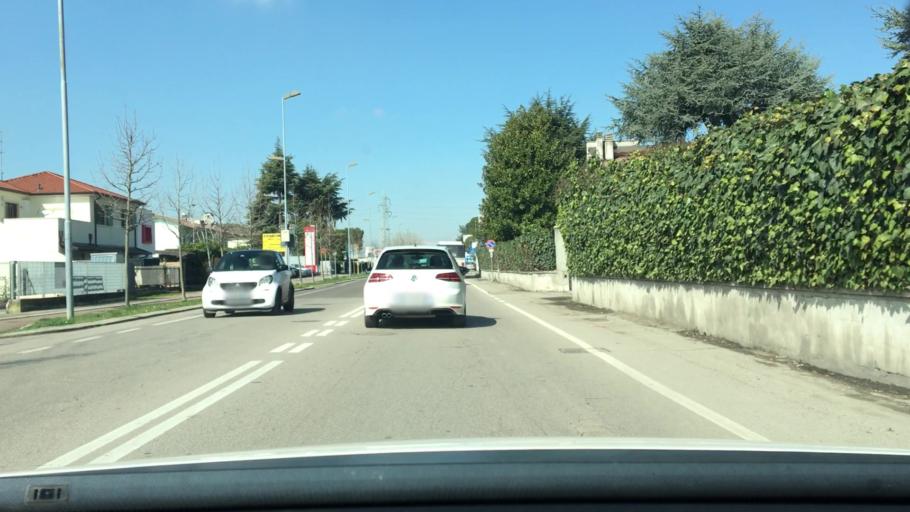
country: IT
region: Veneto
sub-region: Provincia di Verona
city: San Giovanni Lupatoto
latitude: 45.3950
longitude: 11.0285
